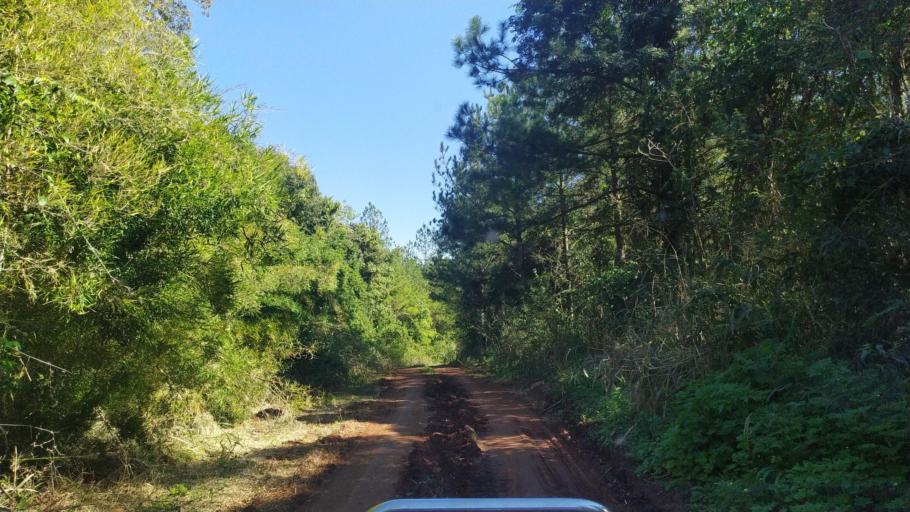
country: AR
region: Misiones
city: El Alcazar
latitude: -26.7586
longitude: -54.5907
